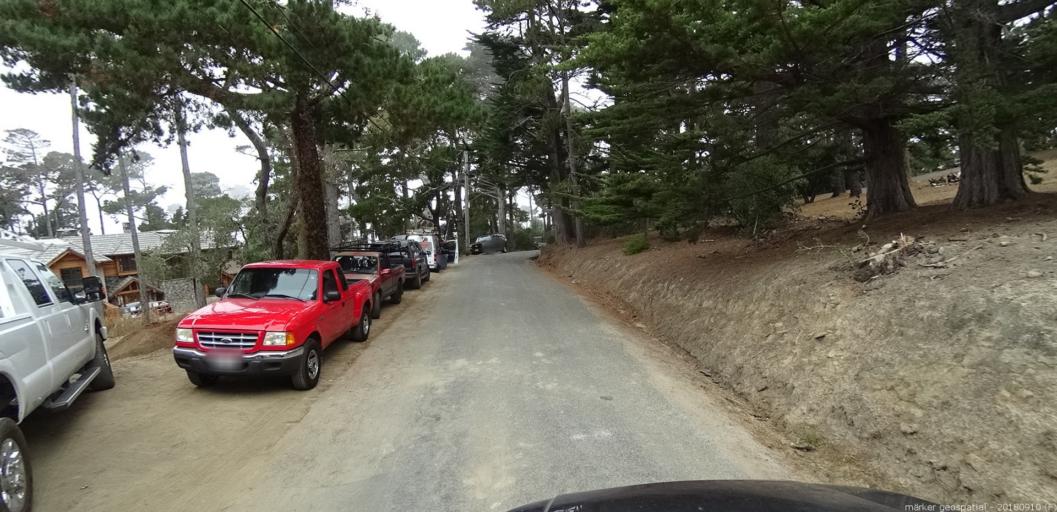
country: US
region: California
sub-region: Monterey County
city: Carmel-by-the-Sea
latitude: 36.4934
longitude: -121.9341
